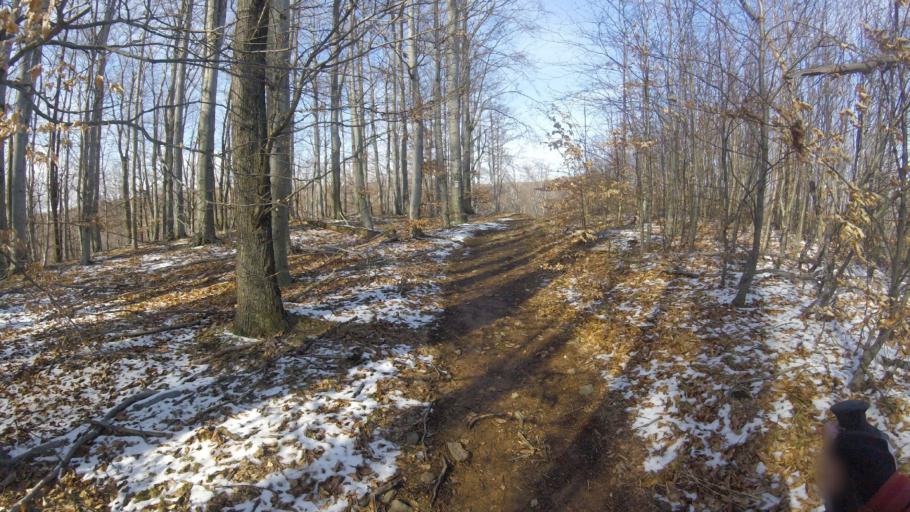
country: HU
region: Heves
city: Paradsasvar
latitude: 47.9041
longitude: 19.9542
